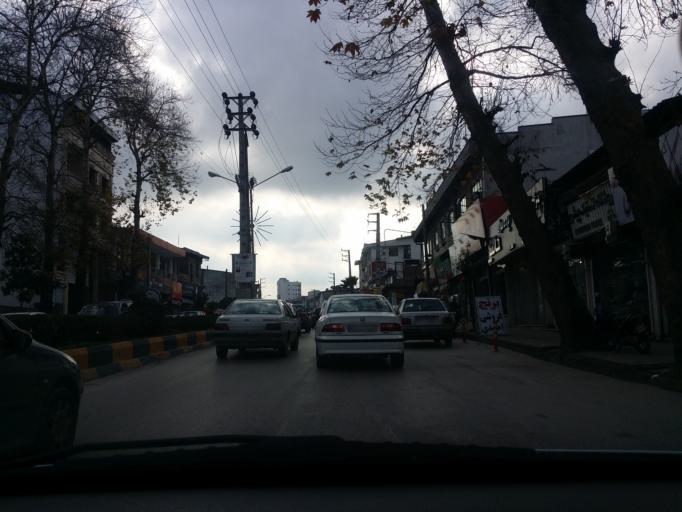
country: IR
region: Mazandaran
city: Chalus
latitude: 36.6603
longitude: 51.4134
